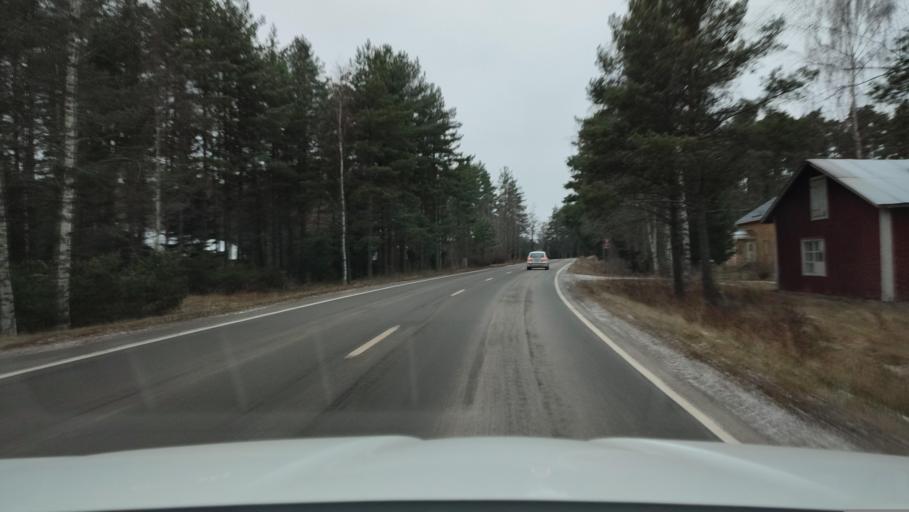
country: FI
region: Ostrobothnia
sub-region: Sydosterbotten
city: Naerpes
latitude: 62.3962
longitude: 21.3685
